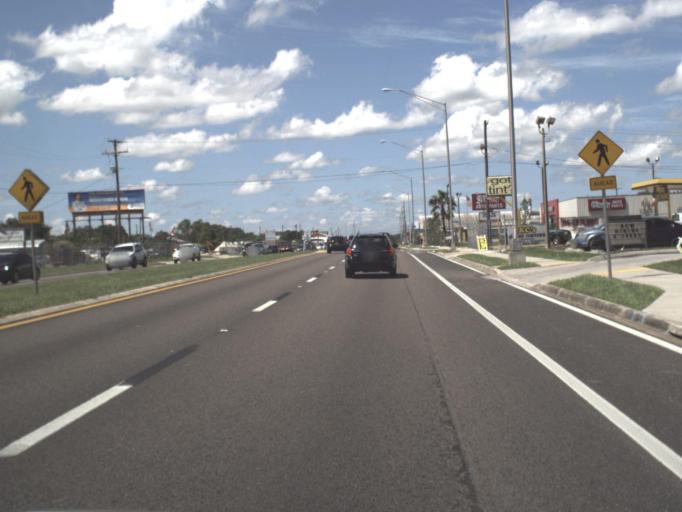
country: US
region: Florida
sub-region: Polk County
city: Combee Settlement
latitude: 28.0480
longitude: -81.9110
